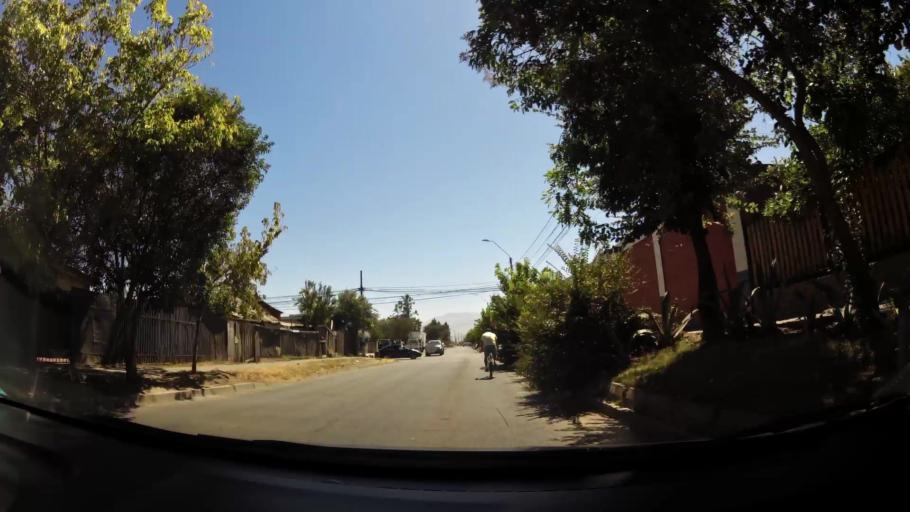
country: CL
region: O'Higgins
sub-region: Provincia de Cachapoal
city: Rancagua
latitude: -34.1676
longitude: -70.7116
